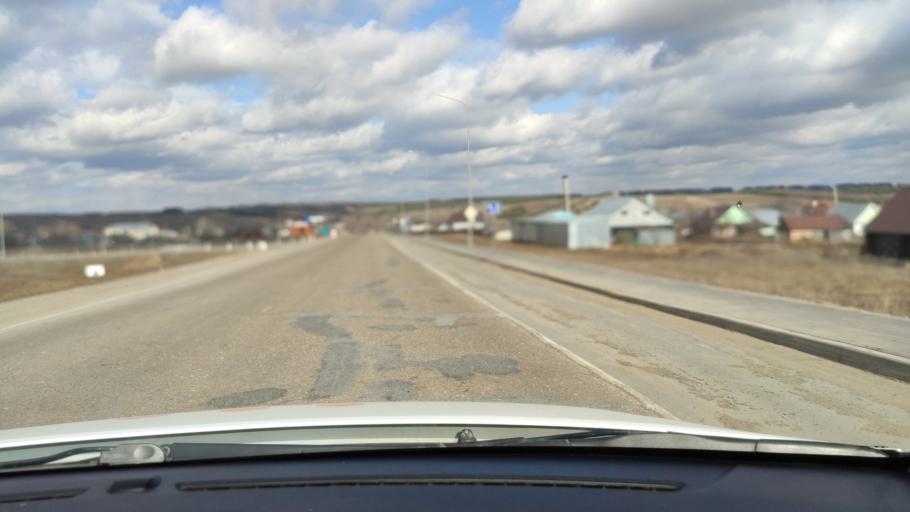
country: RU
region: Tatarstan
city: Vysokaya Gora
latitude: 56.1185
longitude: 49.1944
